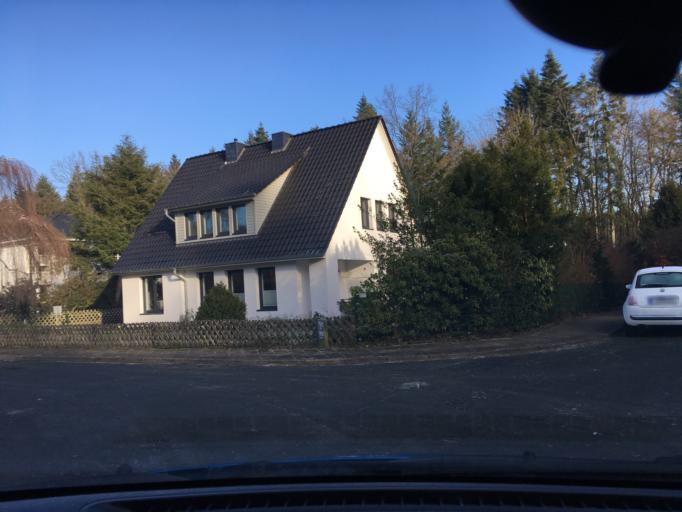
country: DE
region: Lower Saxony
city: Deutsch Evern
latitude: 53.2207
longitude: 10.4115
